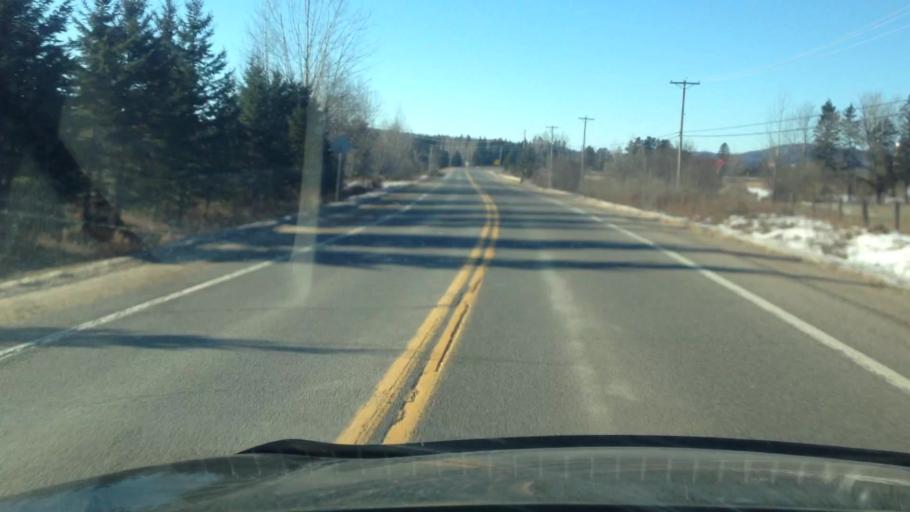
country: CA
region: Quebec
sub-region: Laurentides
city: Mont-Tremblant
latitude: 45.9595
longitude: -74.5726
